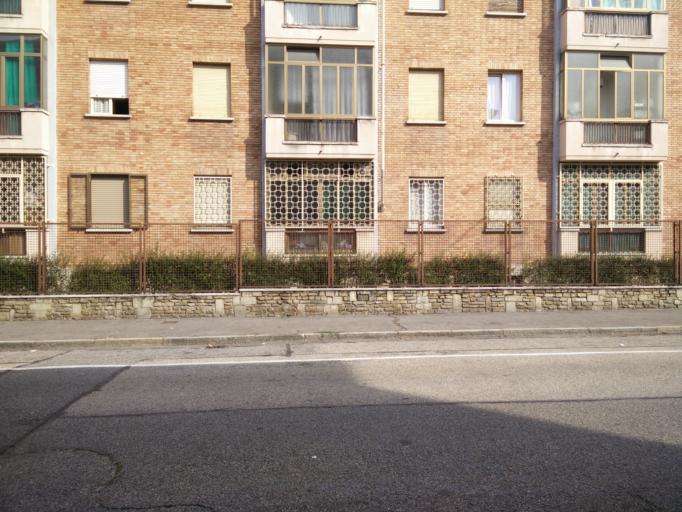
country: IT
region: Piedmont
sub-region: Provincia di Torino
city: Nichelino
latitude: 45.0159
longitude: 7.6516
